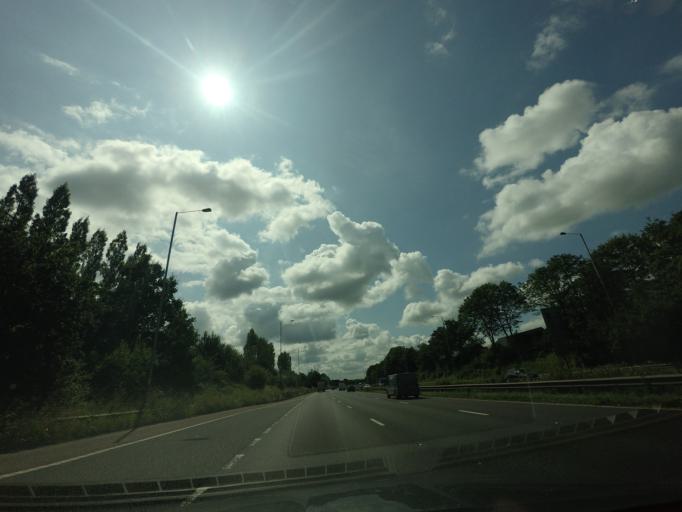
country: GB
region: England
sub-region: Lancashire
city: Clayton-le-Woods
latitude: 53.6911
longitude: -2.6775
